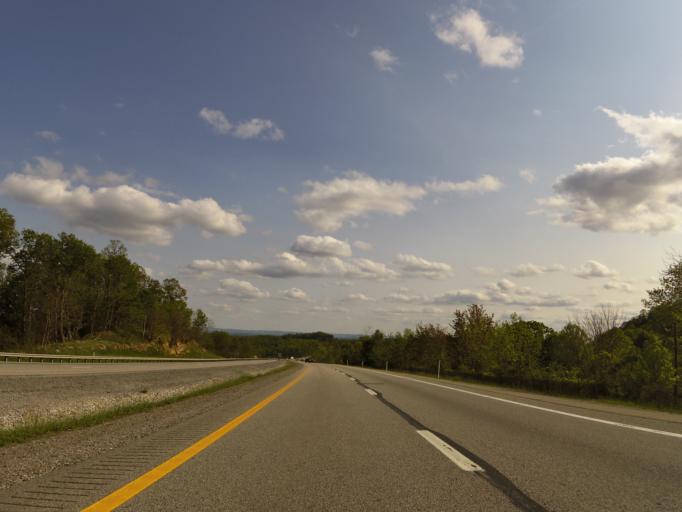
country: US
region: West Virginia
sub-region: Raleigh County
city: Shady Spring
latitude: 37.5619
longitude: -81.1128
